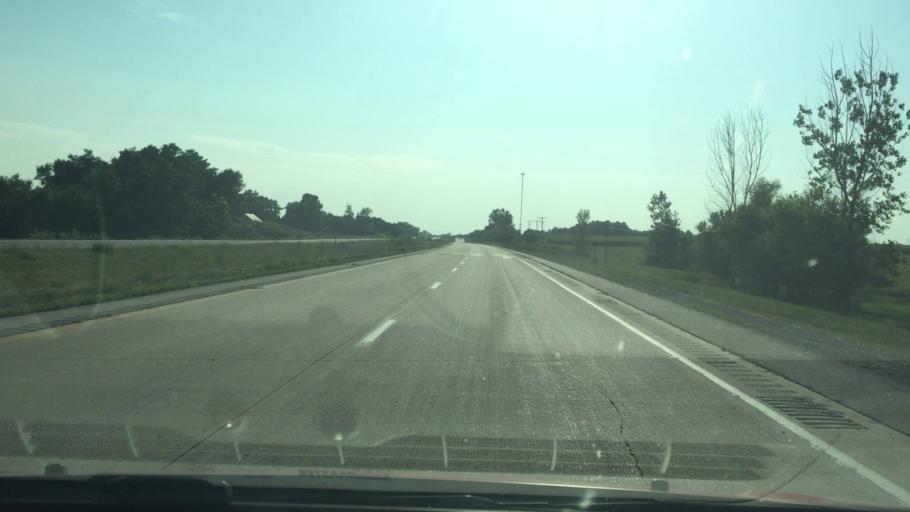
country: US
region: Iowa
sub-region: Cedar County
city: Durant
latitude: 41.5193
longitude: -90.8851
